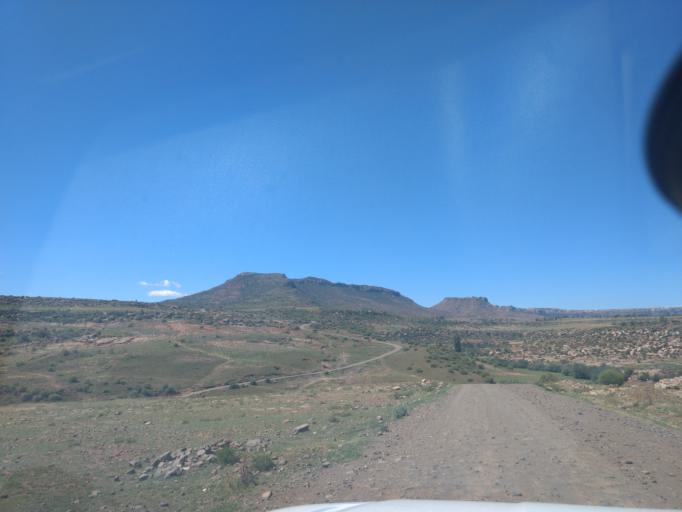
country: LS
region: Maseru
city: Maseru
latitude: -29.4849
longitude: 27.3699
